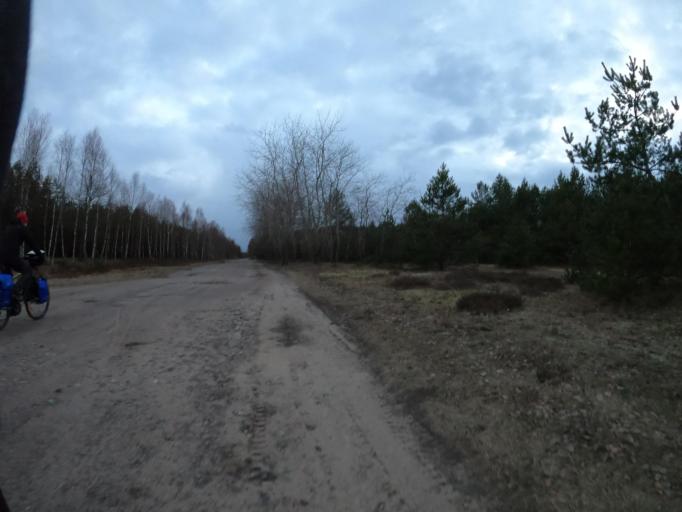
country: PL
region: West Pomeranian Voivodeship
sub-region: Powiat szczecinecki
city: Borne Sulinowo
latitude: 53.5396
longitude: 16.5801
